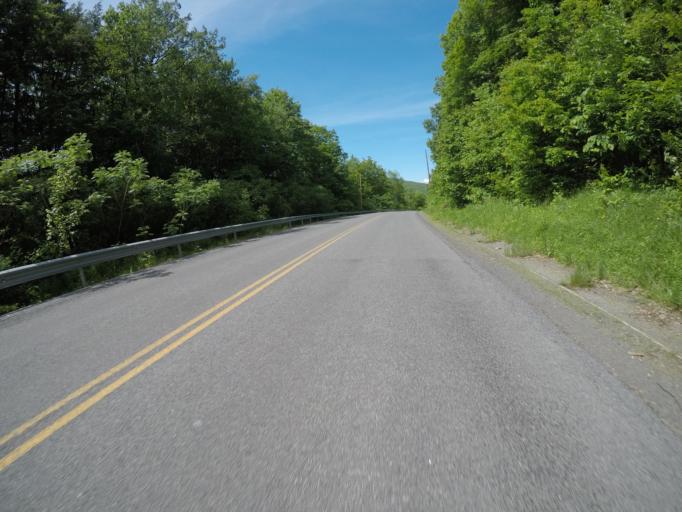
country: US
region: New York
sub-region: Sullivan County
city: Livingston Manor
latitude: 42.0998
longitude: -74.8260
